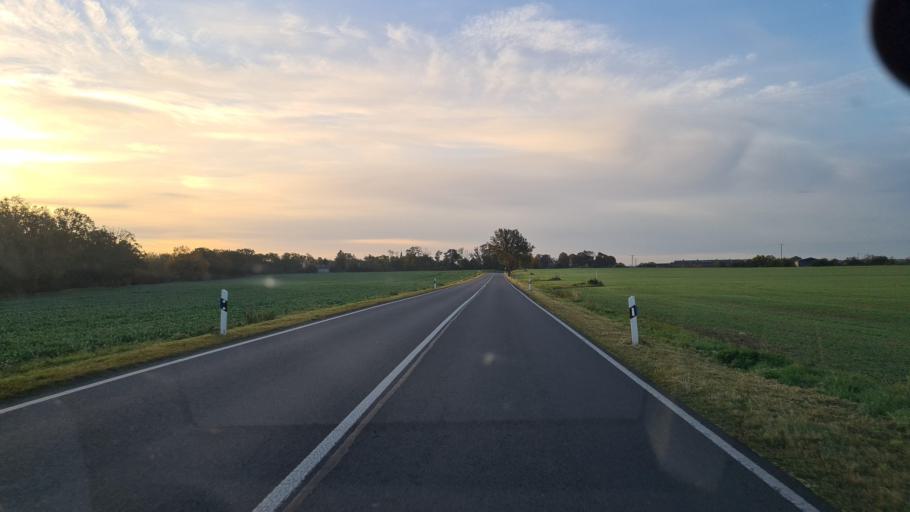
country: DE
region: Saxony
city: Machern
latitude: 51.4075
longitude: 12.6422
